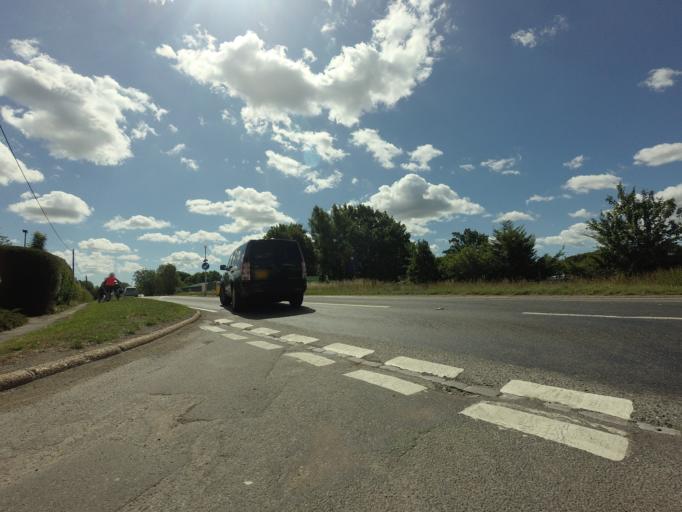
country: GB
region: England
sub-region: East Sussex
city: Horam
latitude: 50.8912
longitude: 0.1840
